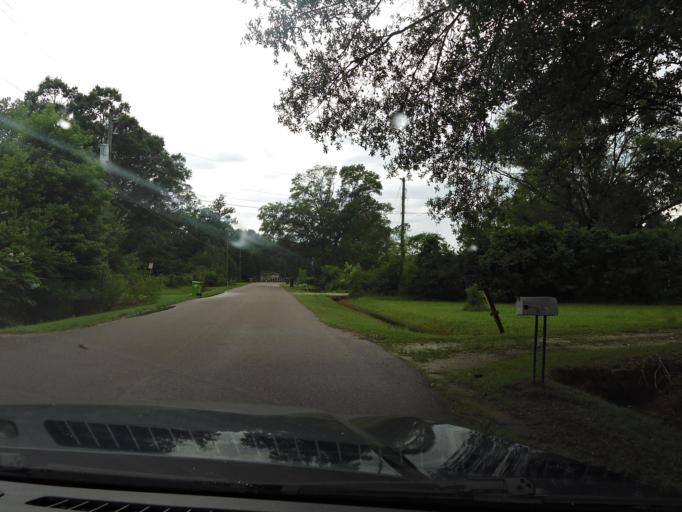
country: US
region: Florida
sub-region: Nassau County
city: Nassau Village-Ratliff
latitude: 30.5084
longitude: -81.8022
